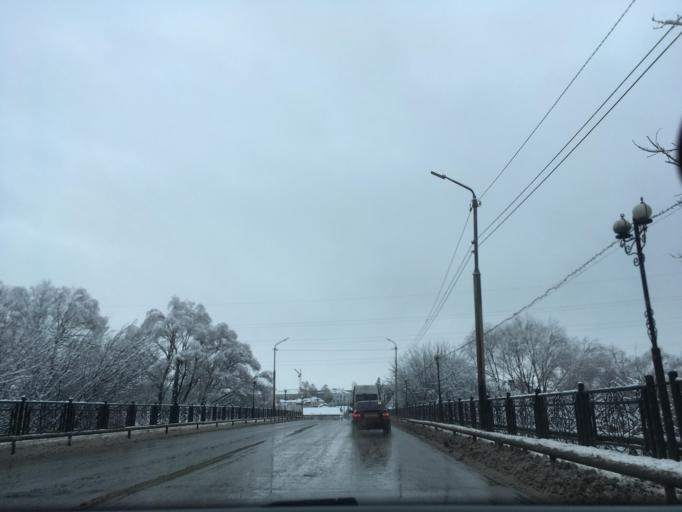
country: RU
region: Voronezj
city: Rossosh'
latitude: 50.2003
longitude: 39.5496
